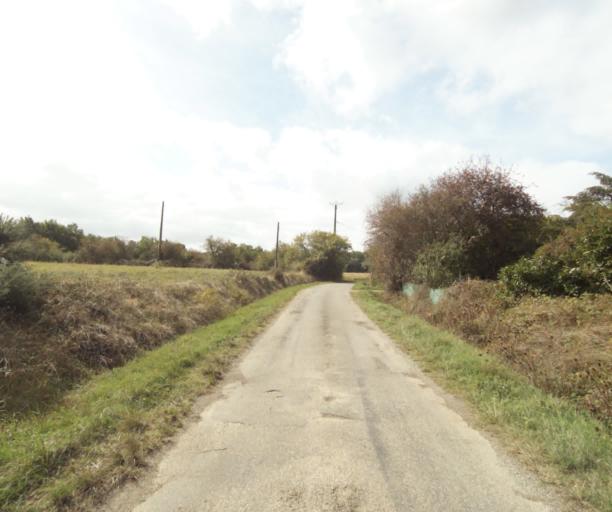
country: FR
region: Midi-Pyrenees
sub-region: Departement du Tarn-et-Garonne
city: Finhan
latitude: 43.8858
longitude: 1.1269
